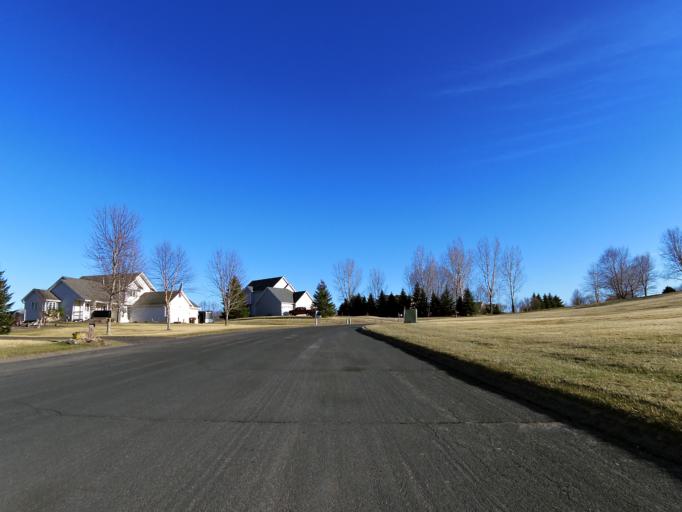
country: US
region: Minnesota
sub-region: Washington County
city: Lakeland
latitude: 44.9735
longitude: -92.8048
